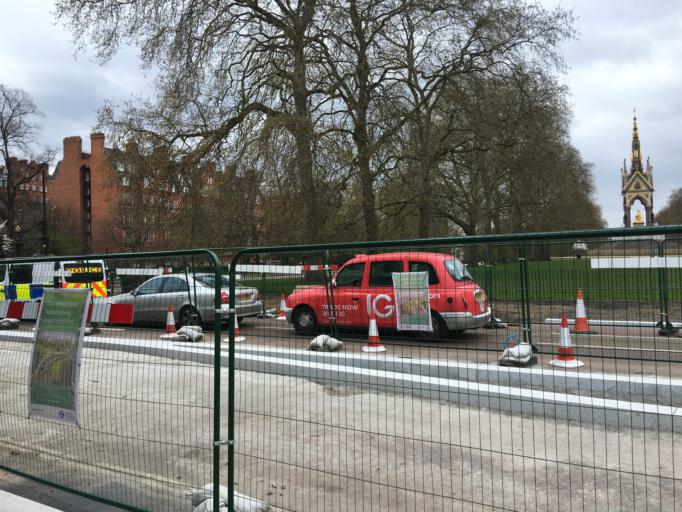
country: GB
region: England
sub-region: Greater London
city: Bayswater
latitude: 51.5026
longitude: -0.1745
